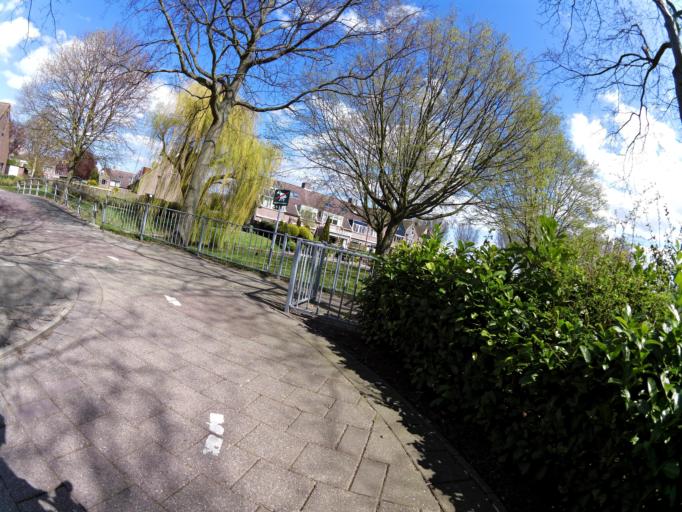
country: NL
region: South Holland
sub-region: Gemeente Brielle
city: Brielle
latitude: 51.8907
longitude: 4.1673
